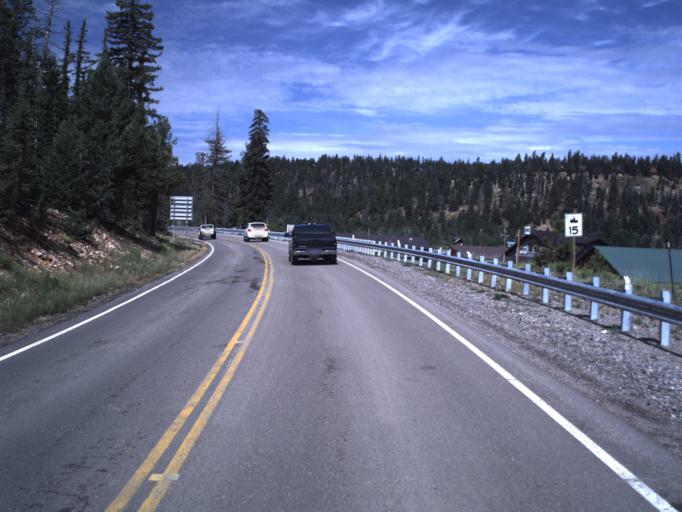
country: US
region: Utah
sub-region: Iron County
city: Parowan
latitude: 37.5248
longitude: -112.6622
